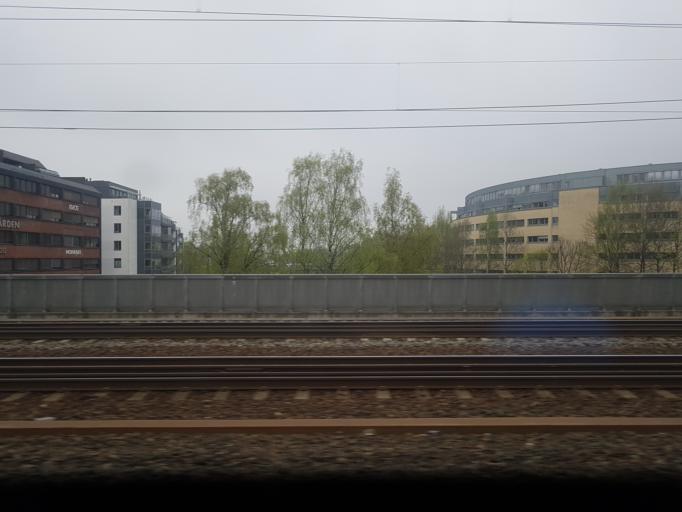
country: NO
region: Akershus
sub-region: Baerum
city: Sandvika
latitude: 59.8924
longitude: 10.5227
